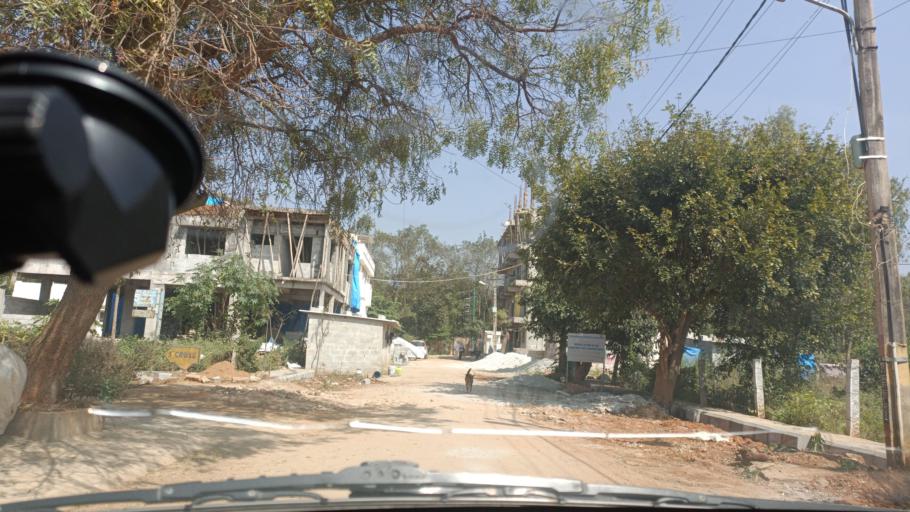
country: IN
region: Karnataka
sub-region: Bangalore Urban
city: Yelahanka
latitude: 13.1224
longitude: 77.6083
